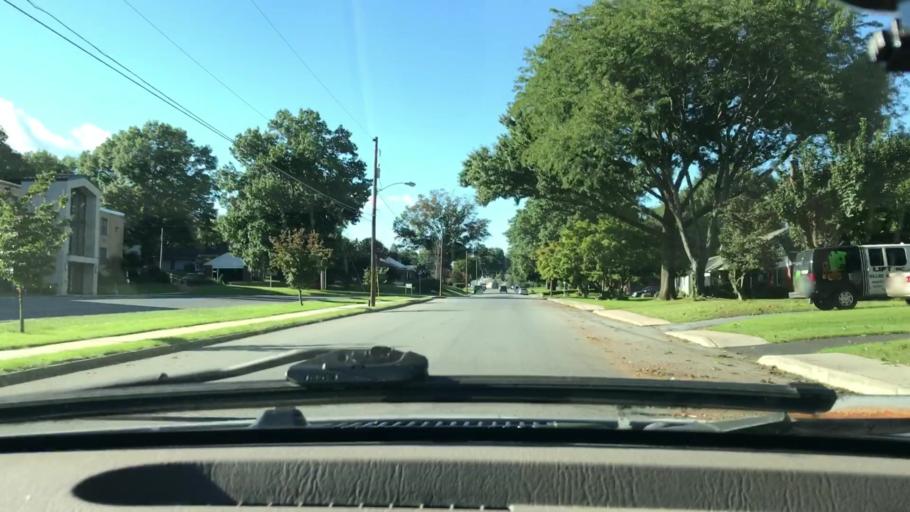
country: US
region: Pennsylvania
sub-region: Lancaster County
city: Elizabethtown
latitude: 40.1579
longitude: -76.6037
